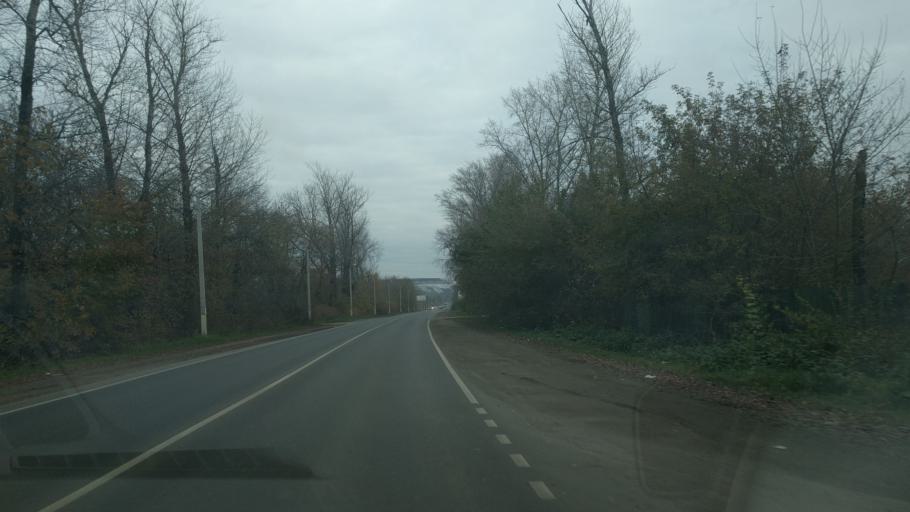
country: RU
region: Moskovskaya
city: Lopatinskiy
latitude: 55.3302
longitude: 38.7142
